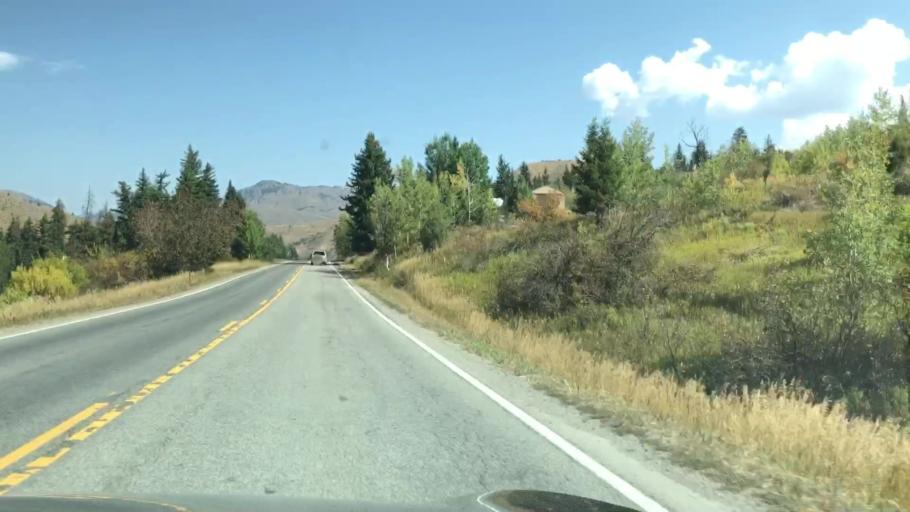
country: US
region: Wyoming
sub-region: Teton County
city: Hoback
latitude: 43.3360
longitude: -110.7254
